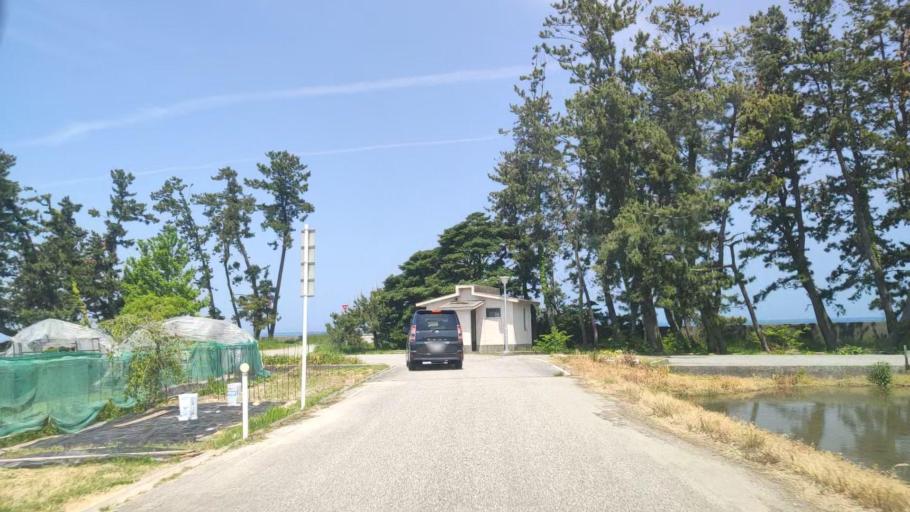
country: JP
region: Toyama
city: Nyuzen
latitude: 36.9624
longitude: 137.5668
